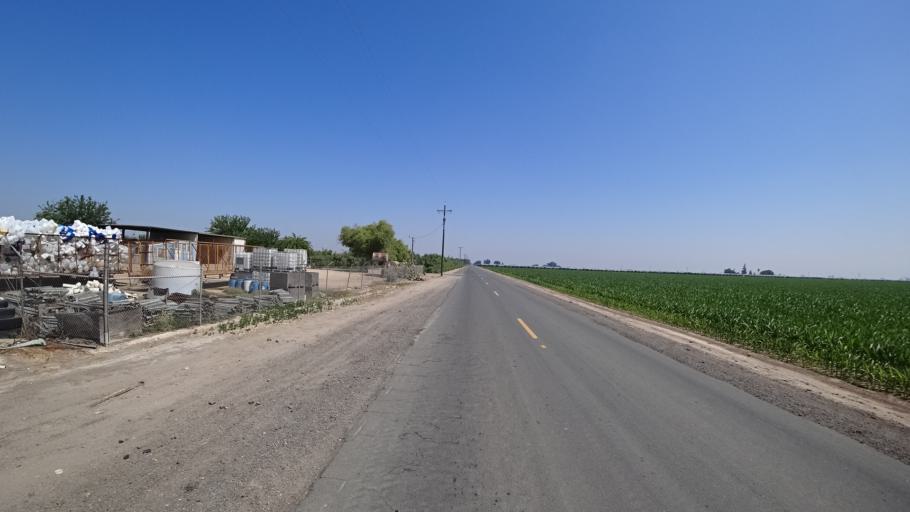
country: US
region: California
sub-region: Fresno County
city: Kingsburg
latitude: 36.4410
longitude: -119.5286
